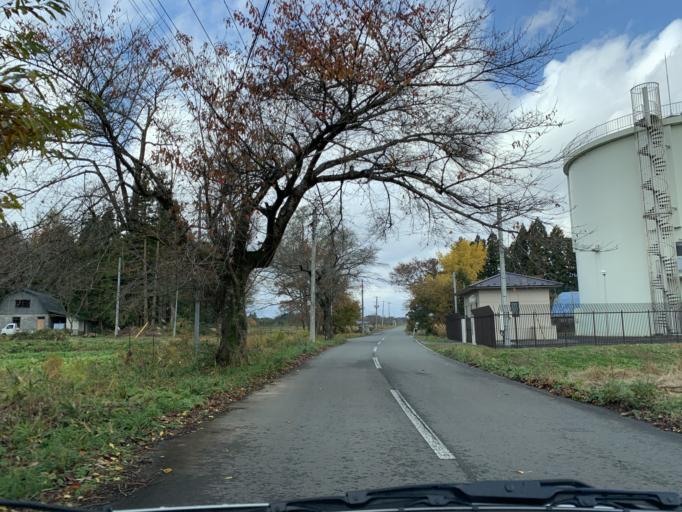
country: JP
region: Iwate
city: Mizusawa
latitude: 39.0654
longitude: 141.0812
